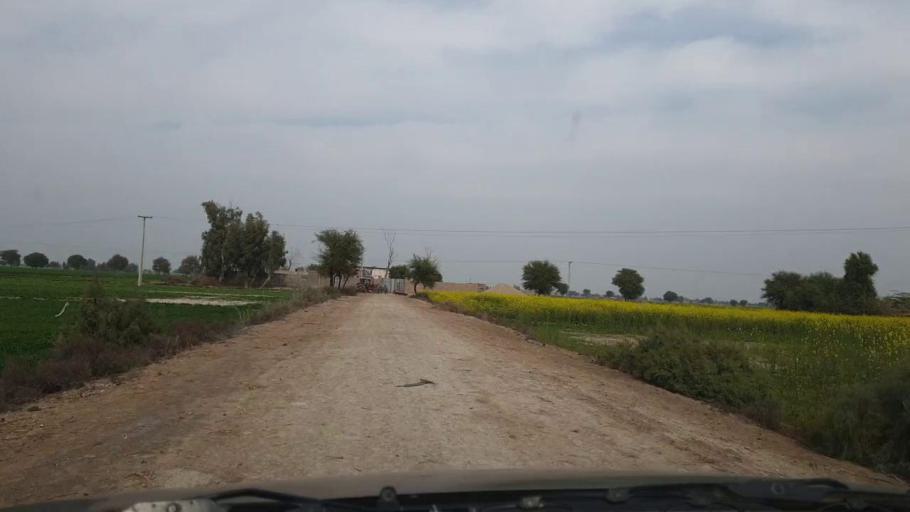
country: PK
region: Sindh
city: Sinjhoro
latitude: 26.0721
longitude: 68.8324
